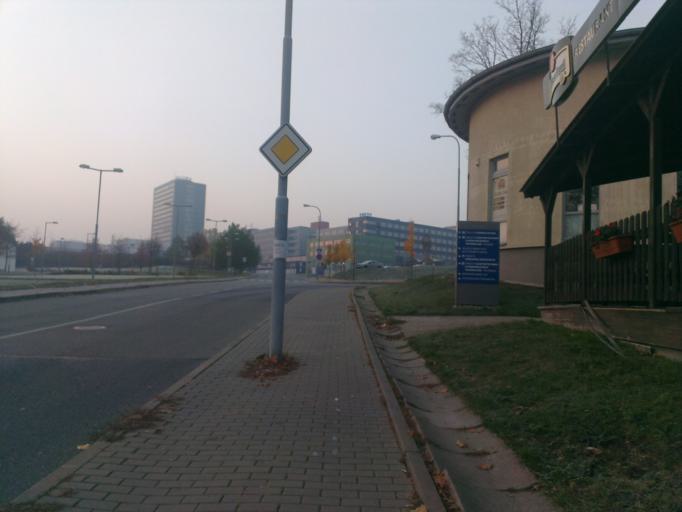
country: CZ
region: South Moravian
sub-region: Mesto Brno
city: Mokra Hora
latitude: 49.2280
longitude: 16.5764
